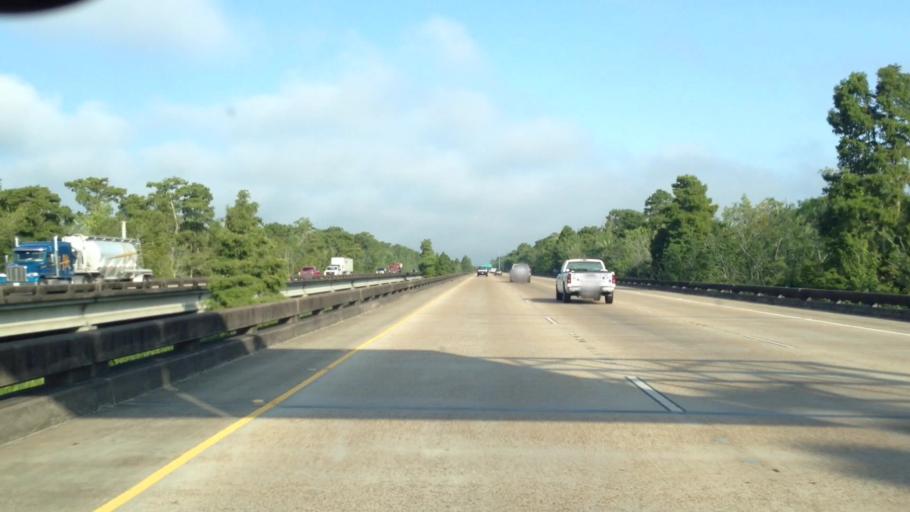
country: US
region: Louisiana
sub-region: Saint John the Baptist Parish
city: Laplace
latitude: 30.0816
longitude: -90.4172
